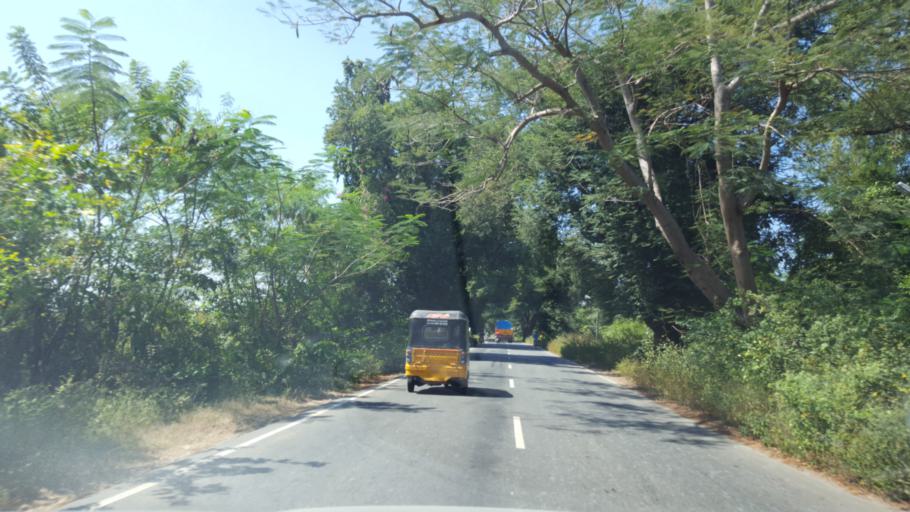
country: IN
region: Tamil Nadu
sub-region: Kancheepuram
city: Chengalpattu
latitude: 12.7363
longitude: 79.9435
